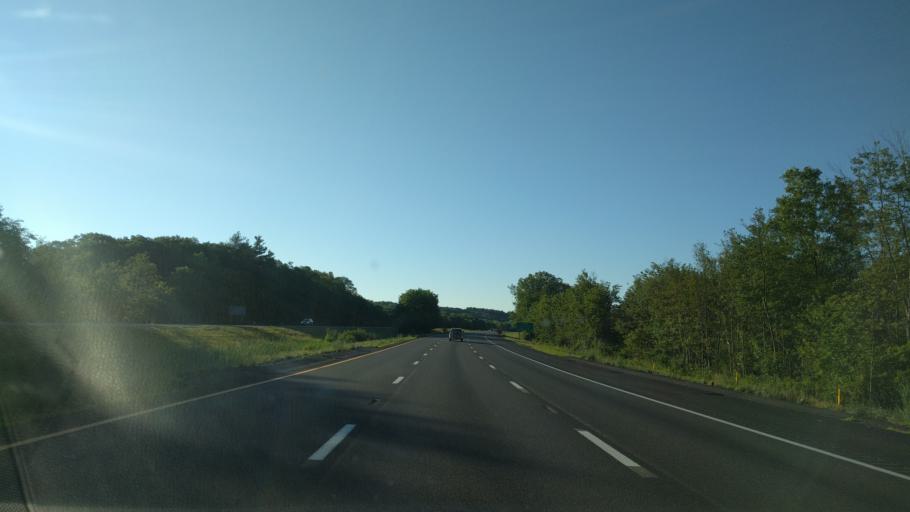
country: US
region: Massachusetts
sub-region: Norfolk County
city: Bellingham
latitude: 42.1016
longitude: -71.4427
